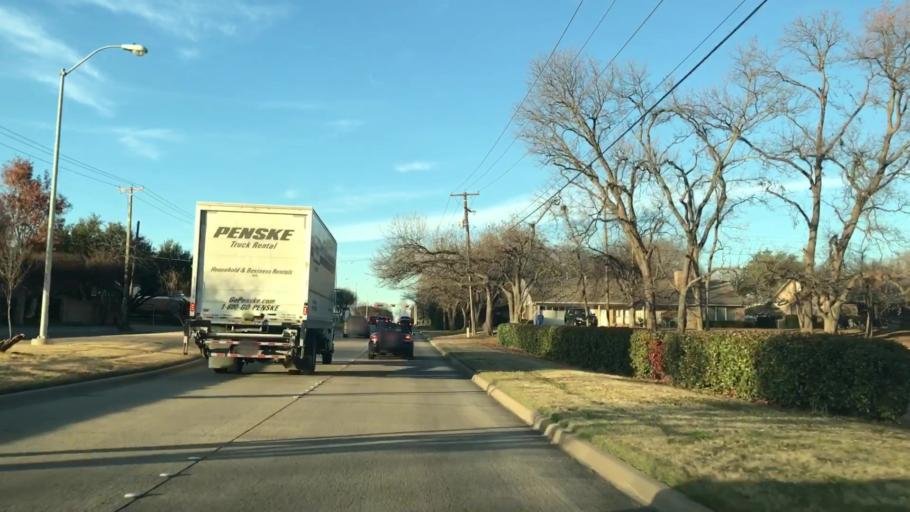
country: US
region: Texas
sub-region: Dallas County
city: Rowlett
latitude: 32.8898
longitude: -96.5181
